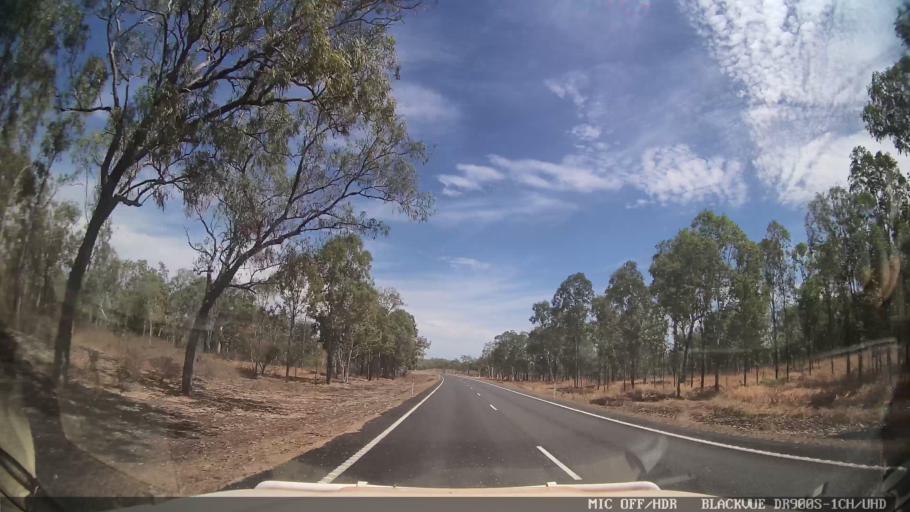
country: AU
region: Queensland
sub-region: Cook
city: Cooktown
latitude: -15.7579
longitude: 145.0024
